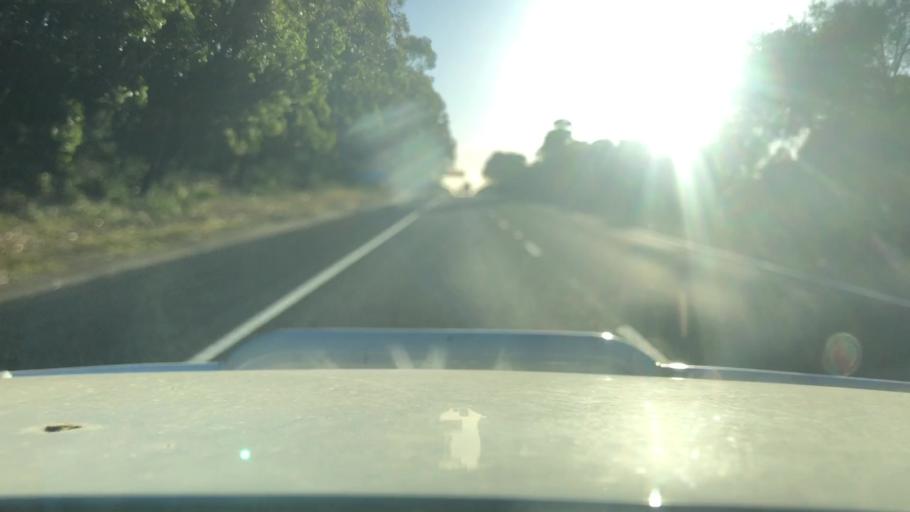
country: AU
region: New South Wales
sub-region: Wingecarribee
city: Bundanoon
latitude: -34.6212
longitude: 150.2098
